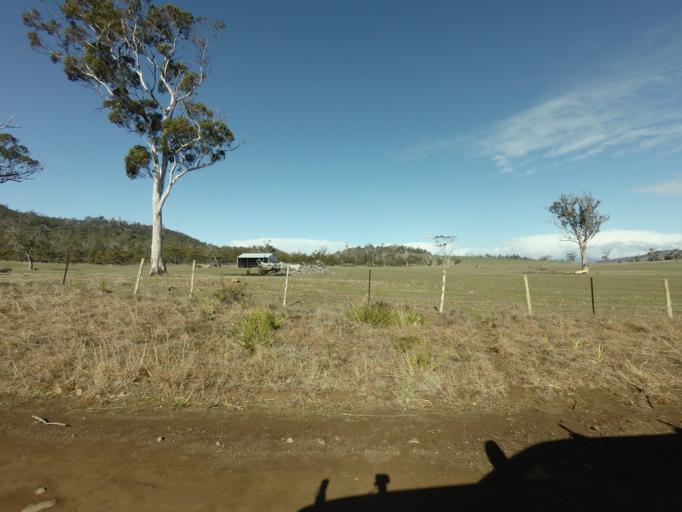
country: AU
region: Tasmania
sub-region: Sorell
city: Sorell
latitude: -42.4167
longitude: 147.9388
